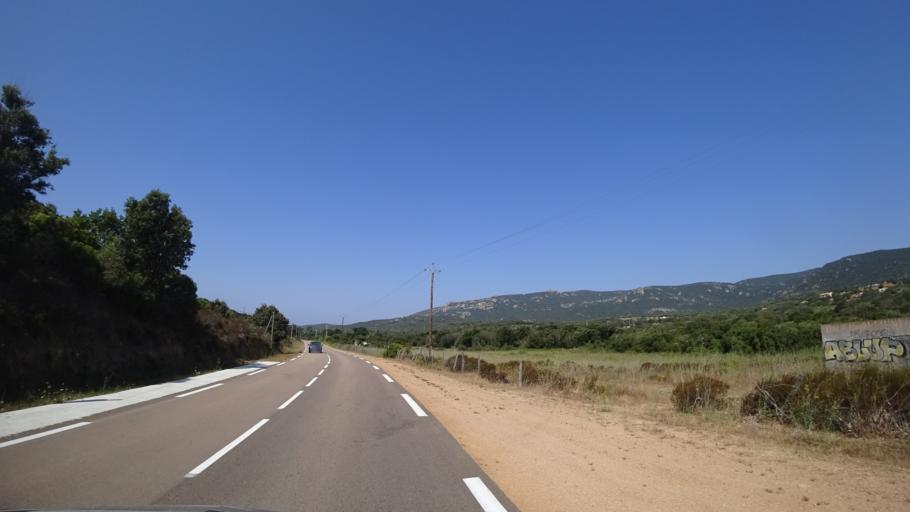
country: FR
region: Corsica
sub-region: Departement de la Corse-du-Sud
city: Sartene
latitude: 41.5026
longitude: 9.0134
